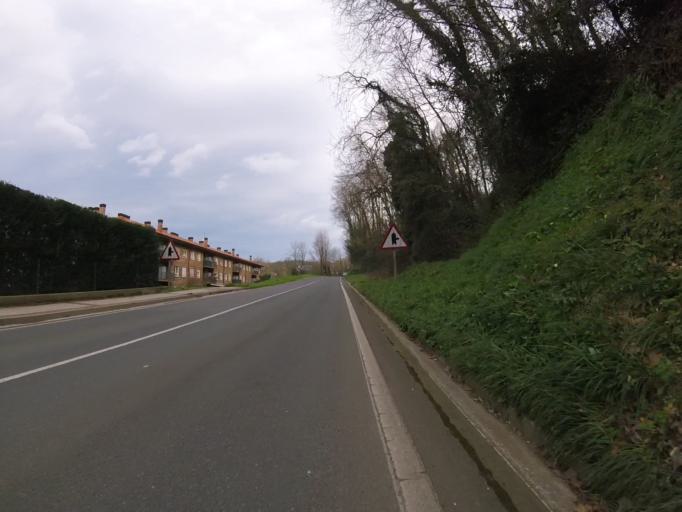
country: ES
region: Basque Country
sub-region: Provincia de Guipuzcoa
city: Cestona
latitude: 43.2543
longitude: -2.2593
